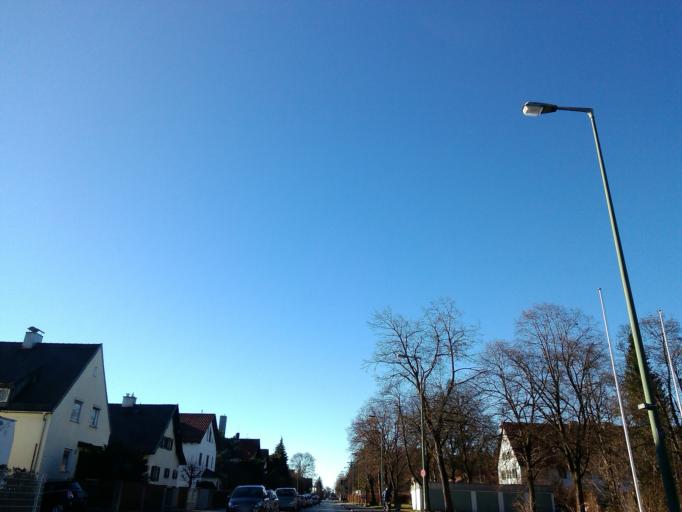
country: DE
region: Bavaria
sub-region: Upper Bavaria
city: Pasing
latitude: 48.1651
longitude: 11.4529
